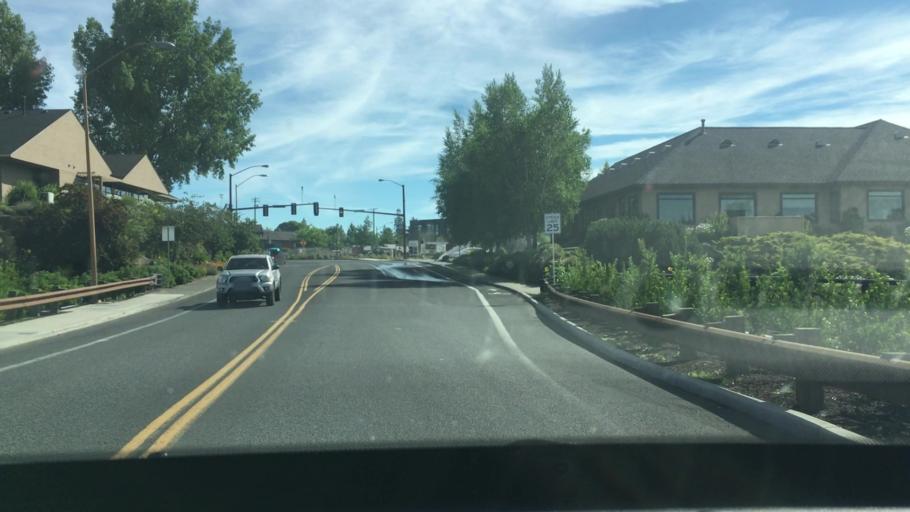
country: US
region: Oregon
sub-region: Deschutes County
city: Bend
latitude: 44.0501
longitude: -121.3200
